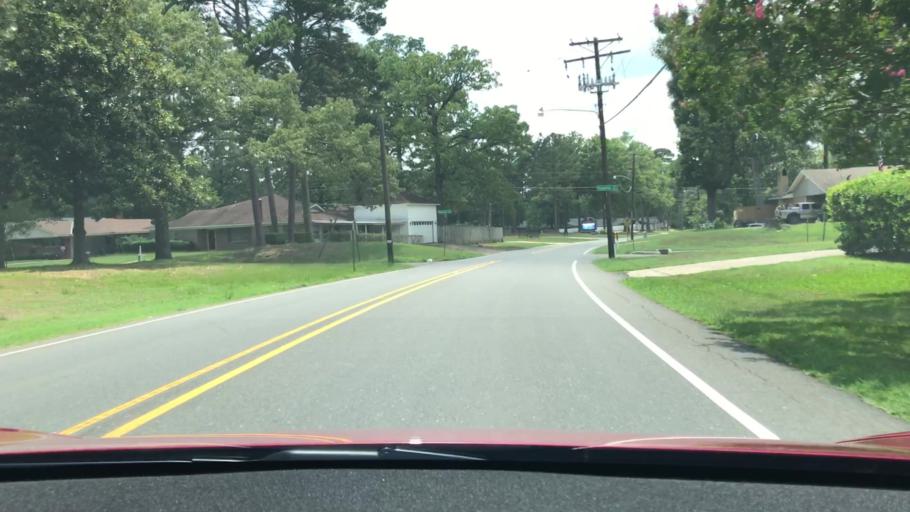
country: US
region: Louisiana
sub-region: De Soto Parish
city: Stonewall
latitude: 32.3893
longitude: -93.7868
